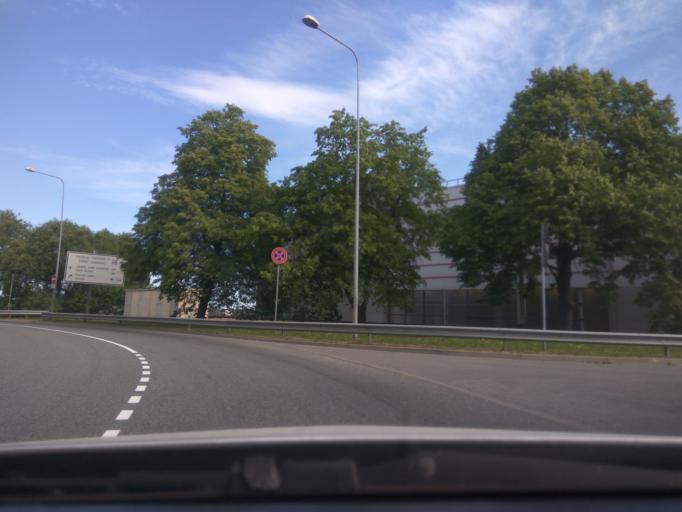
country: LV
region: Ventspils
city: Ventspils
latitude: 57.3897
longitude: 21.5835
